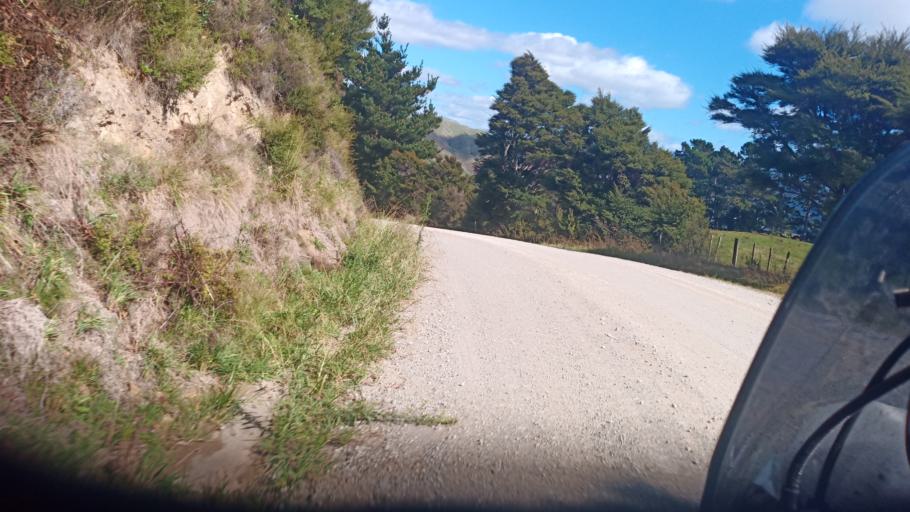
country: NZ
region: Gisborne
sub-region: Gisborne District
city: Gisborne
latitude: -38.3949
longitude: 177.6722
